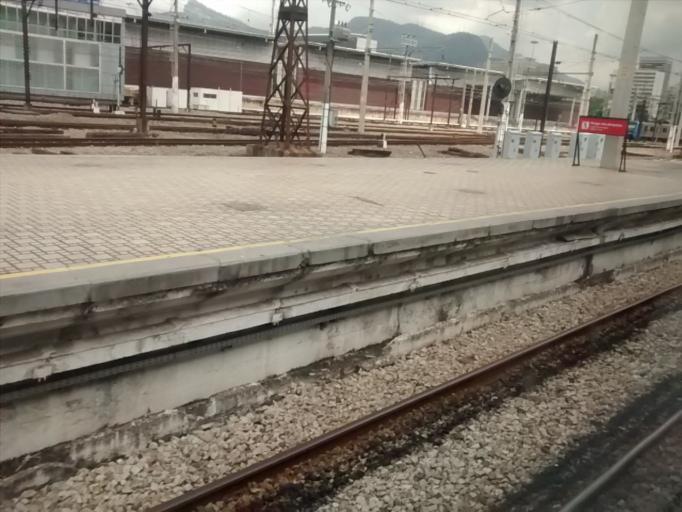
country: BR
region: Rio de Janeiro
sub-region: Rio De Janeiro
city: Rio de Janeiro
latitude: -22.9037
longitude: -43.1945
